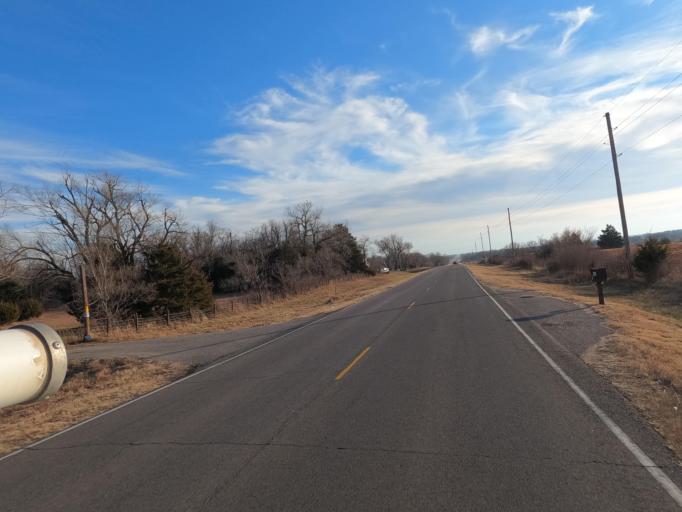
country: US
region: Kansas
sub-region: Reno County
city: Buhler
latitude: 38.0519
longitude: -97.7753
